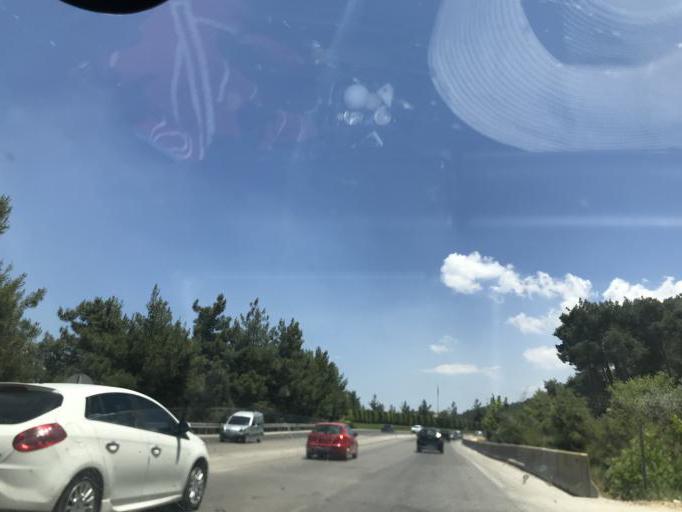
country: TR
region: Denizli
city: Denizli
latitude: 37.7309
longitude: 29.1622
